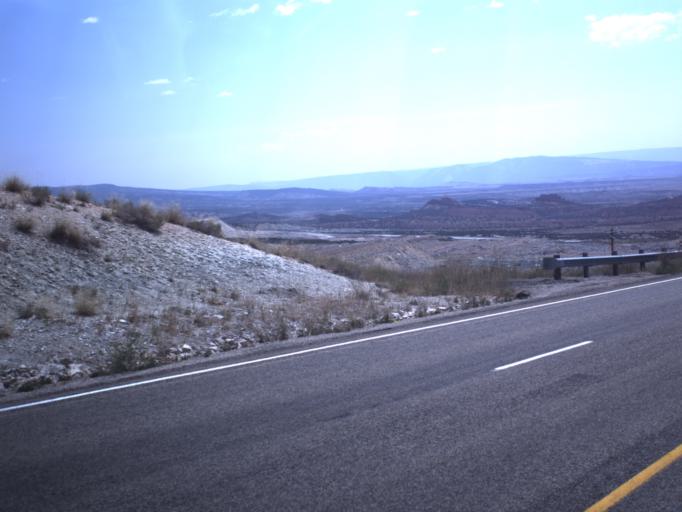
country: US
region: Utah
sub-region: Uintah County
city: Vernal
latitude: 40.6248
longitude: -109.4740
